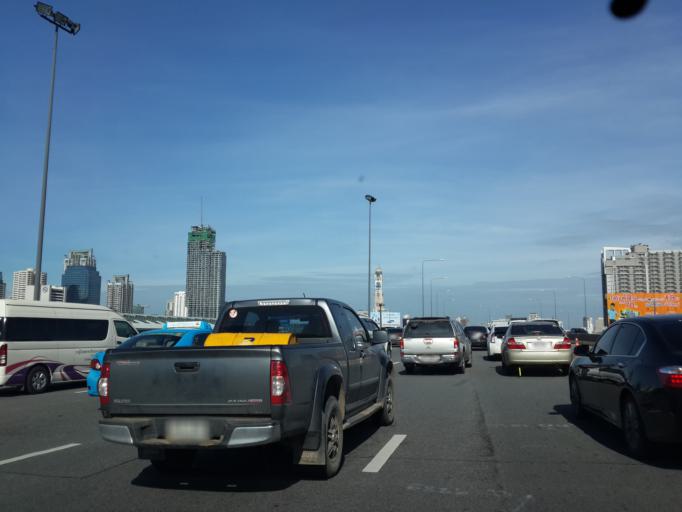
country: TH
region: Bangkok
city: Din Daeng
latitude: 13.7528
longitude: 100.5657
